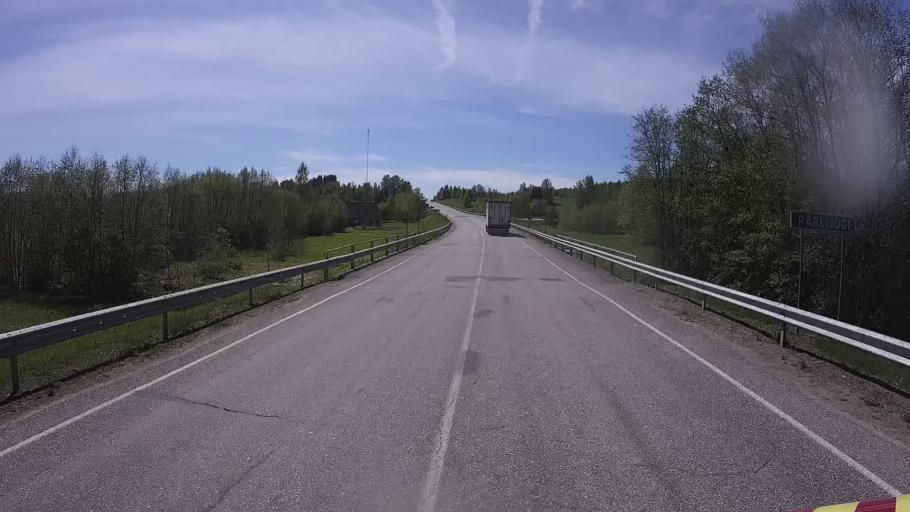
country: LV
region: Apes Novads
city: Ape
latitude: 57.7369
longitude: 26.7899
